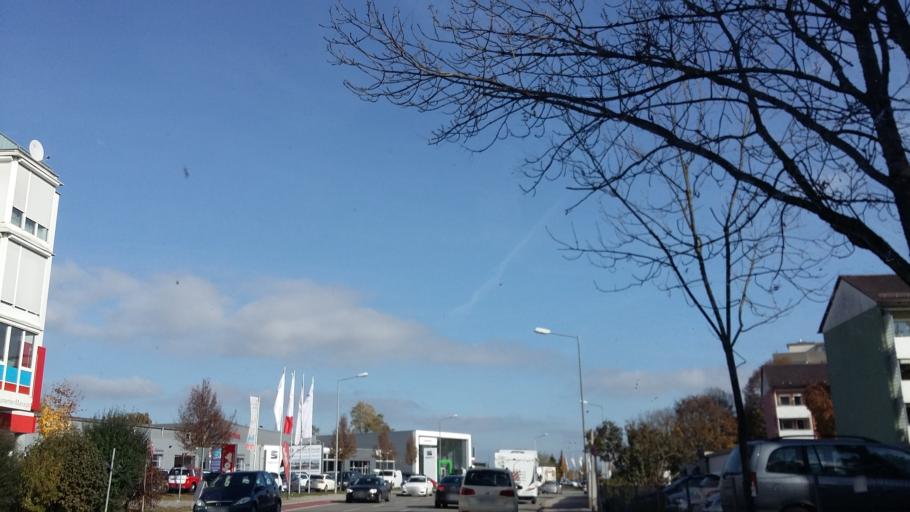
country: DE
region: Bavaria
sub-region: Upper Bavaria
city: Rosenheim
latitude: 47.8518
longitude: 12.0971
